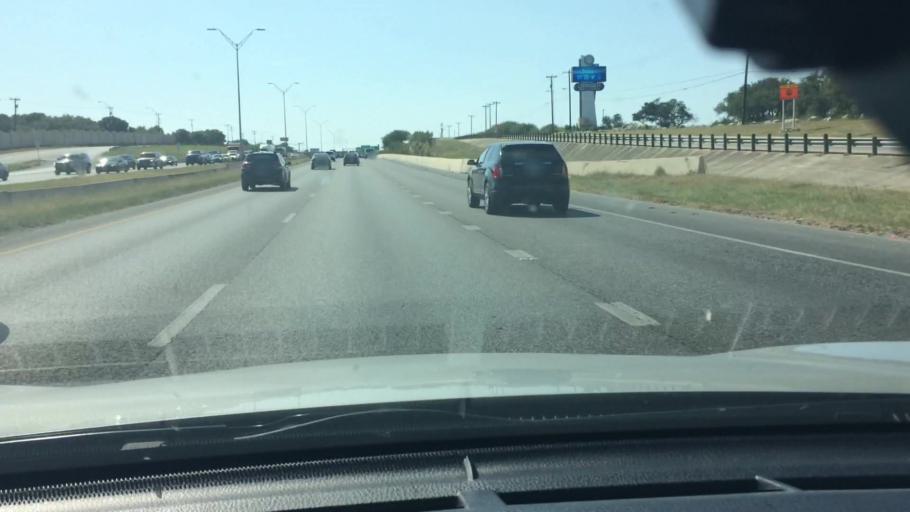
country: US
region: Texas
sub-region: Bexar County
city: Hollywood Park
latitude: 29.6056
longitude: -98.4510
